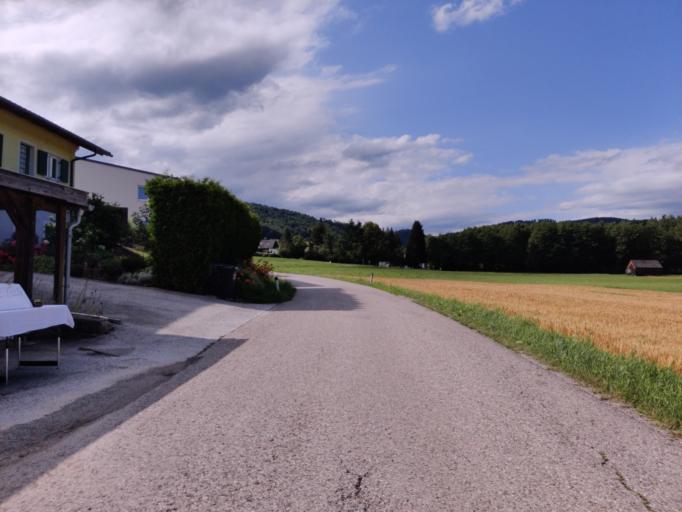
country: AT
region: Styria
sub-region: Politischer Bezirk Graz-Umgebung
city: Thal
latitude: 47.0708
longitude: 15.3366
